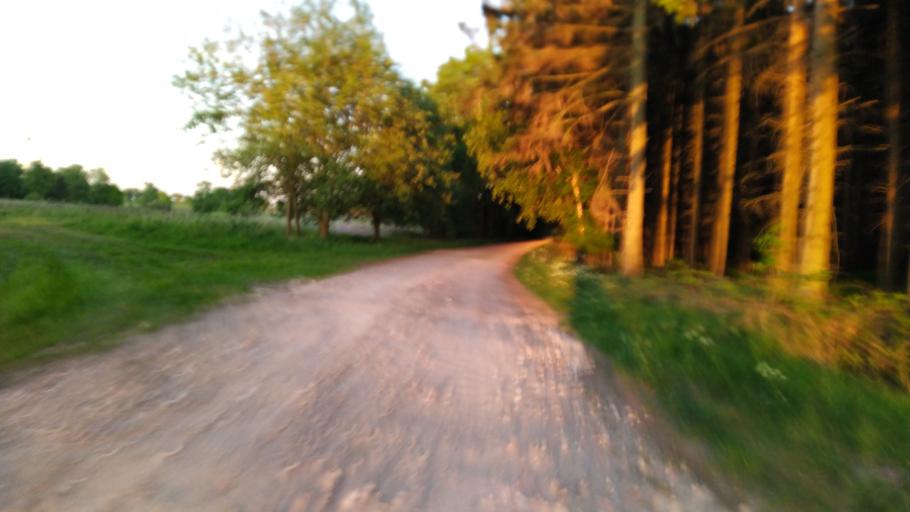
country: DE
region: Lower Saxony
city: Bargstedt
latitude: 53.4890
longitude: 9.4495
